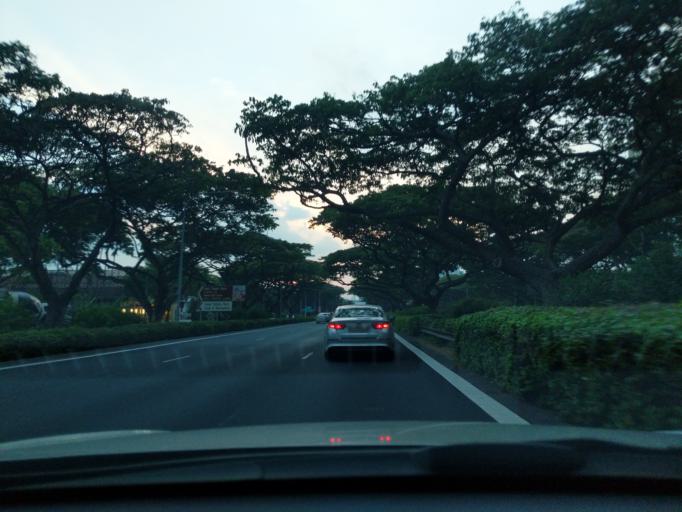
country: SG
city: Singapore
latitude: 1.3023
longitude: 103.9136
